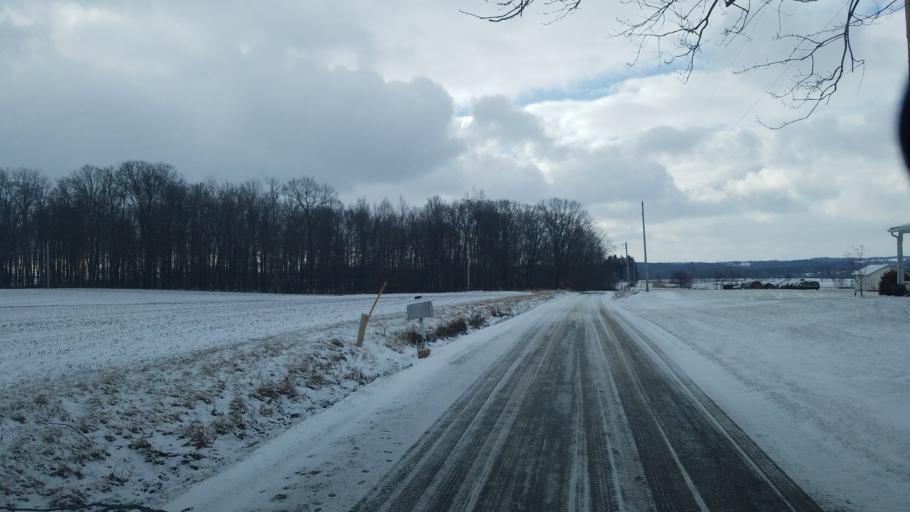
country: US
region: Ohio
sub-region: Knox County
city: Fredericktown
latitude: 40.5441
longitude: -82.5881
